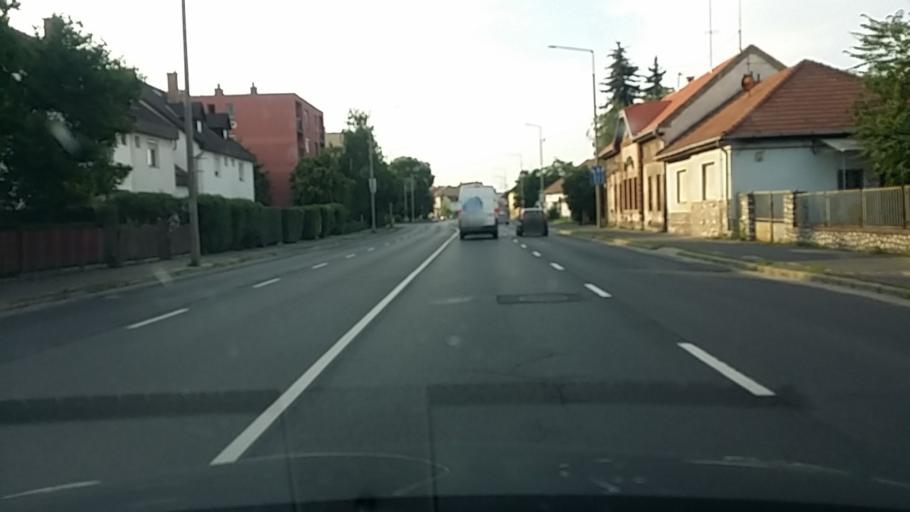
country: HU
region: Borsod-Abauj-Zemplen
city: Miskolc
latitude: 48.0704
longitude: 20.7903
